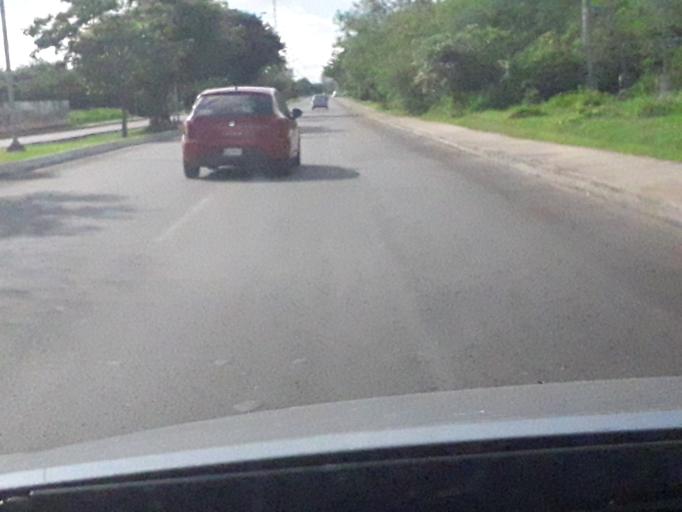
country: MX
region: Yucatan
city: Merida
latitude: 21.0375
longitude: -89.6094
